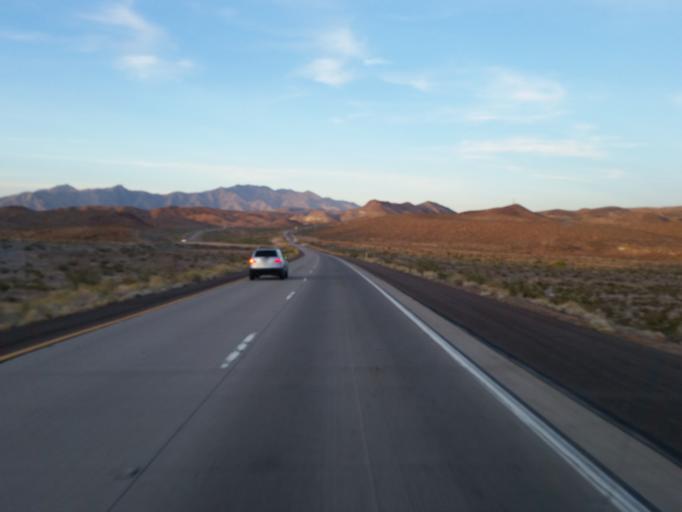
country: US
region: California
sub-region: San Bernardino County
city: Twentynine Palms
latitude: 34.7301
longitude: -115.9023
